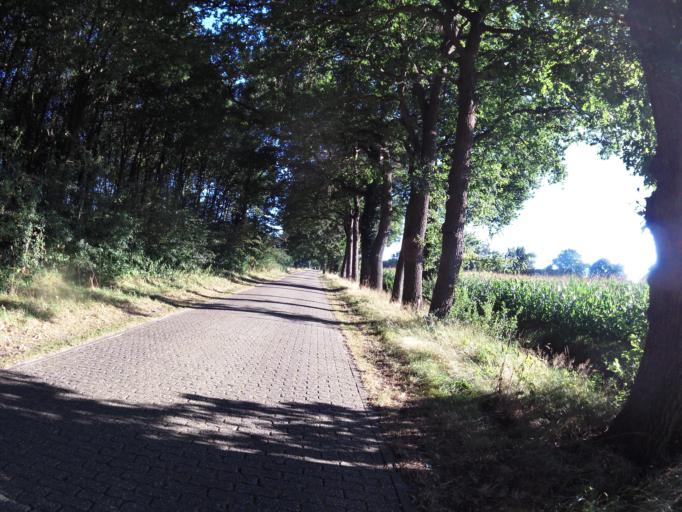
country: NL
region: Gelderland
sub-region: Gemeente Winterswijk
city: Winterswijk
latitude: 51.9408
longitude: 6.7545
